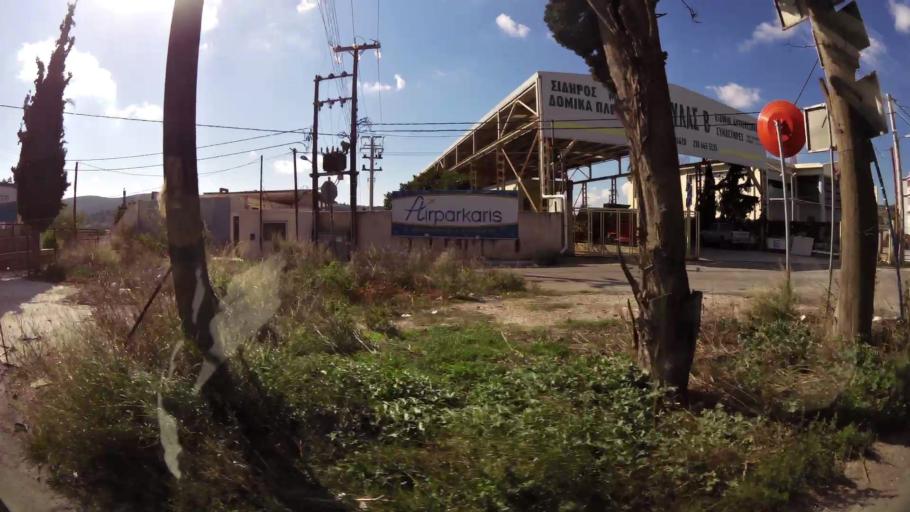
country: GR
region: Attica
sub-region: Nomarchia Anatolikis Attikis
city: Koropi
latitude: 37.8896
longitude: 23.8896
